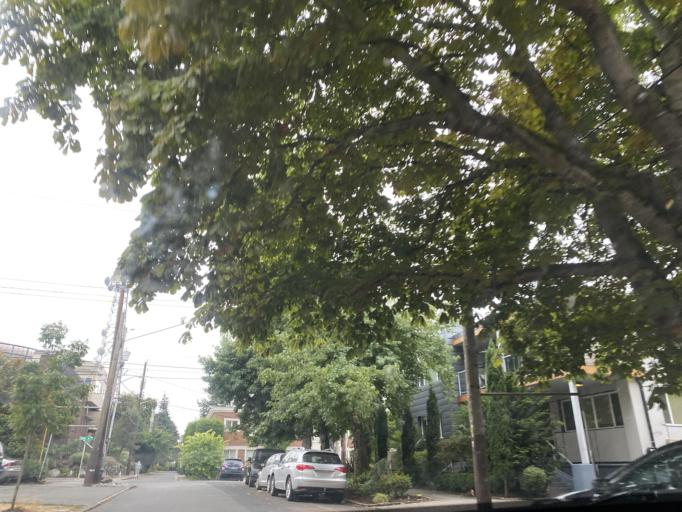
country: US
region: Washington
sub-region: King County
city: Seattle
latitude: 47.6328
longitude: -122.3557
